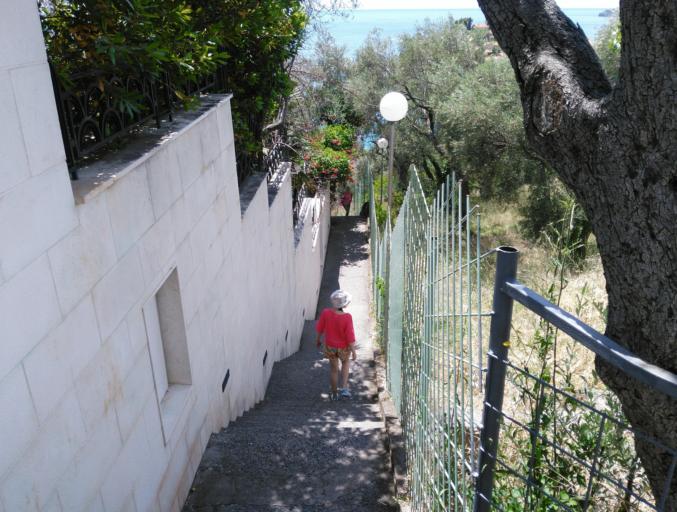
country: ME
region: Budva
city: Budva
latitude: 42.2560
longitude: 18.8968
